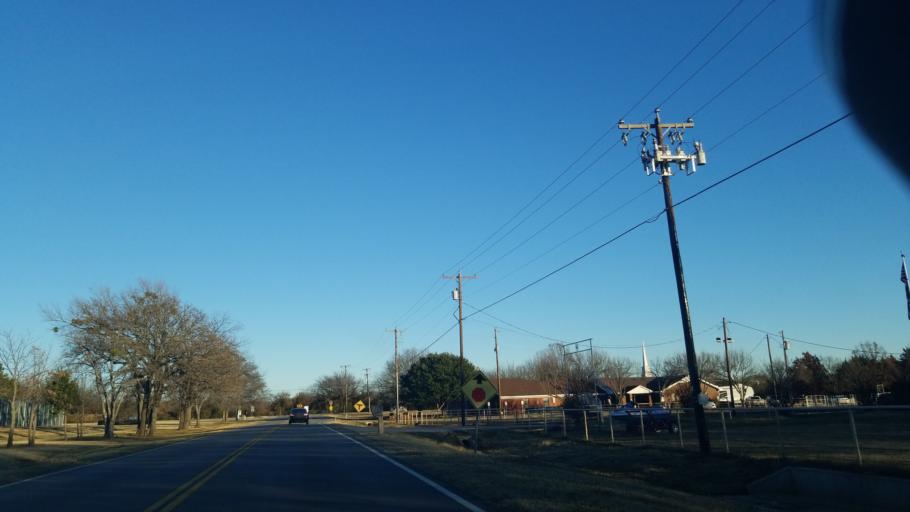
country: US
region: Texas
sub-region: Denton County
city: Shady Shores
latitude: 33.1606
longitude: -97.0424
